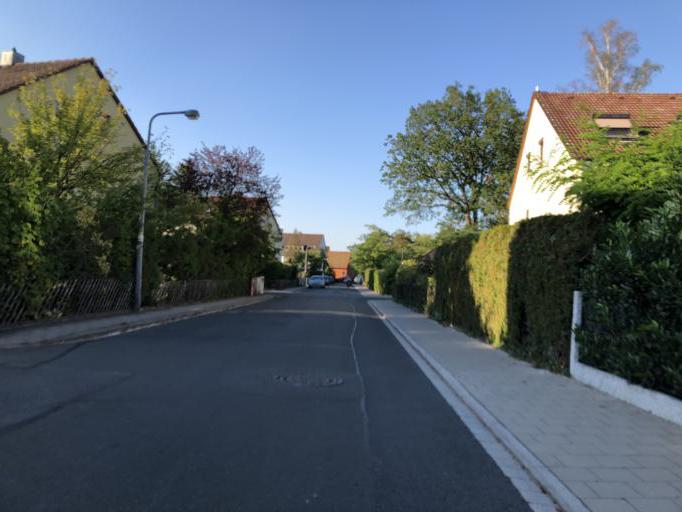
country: DE
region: Bavaria
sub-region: Regierungsbezirk Mittelfranken
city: Buckenhof
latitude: 49.5916
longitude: 11.0496
